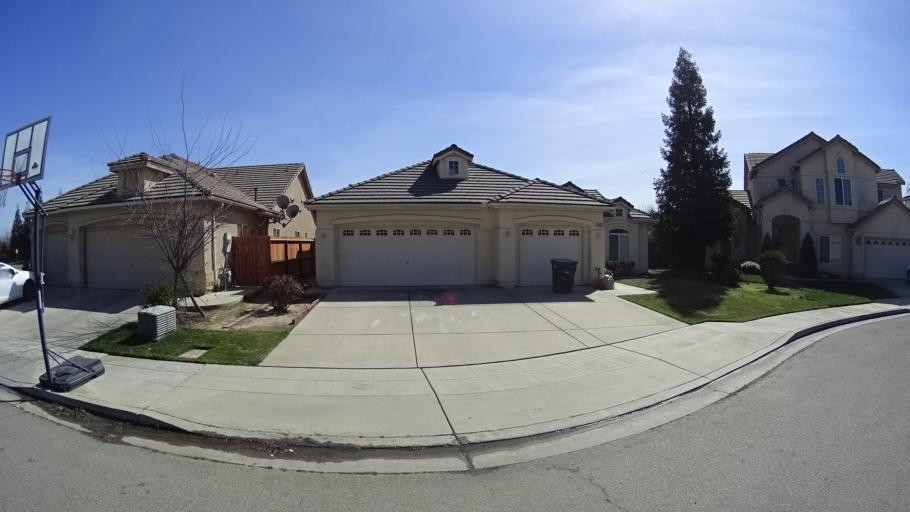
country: US
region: California
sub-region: Fresno County
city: Clovis
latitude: 36.8937
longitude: -119.7619
